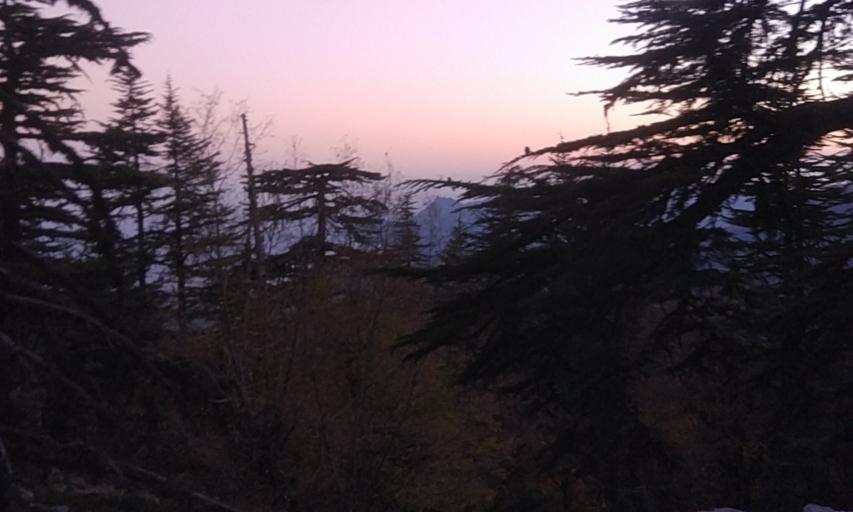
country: TR
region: Antalya
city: Altinyaka
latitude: 36.5346
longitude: 30.4199
